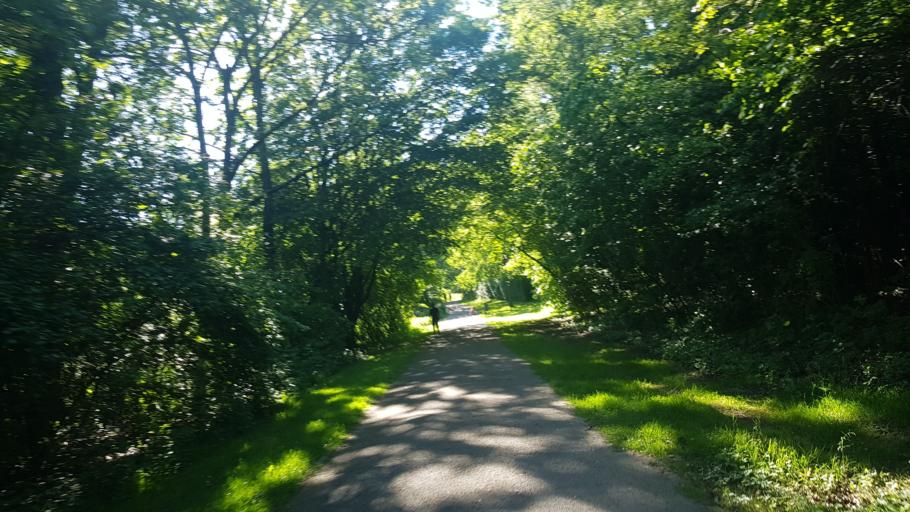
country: DE
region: North Rhine-Westphalia
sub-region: Regierungsbezirk Dusseldorf
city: Essen
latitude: 51.4678
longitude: 7.0528
